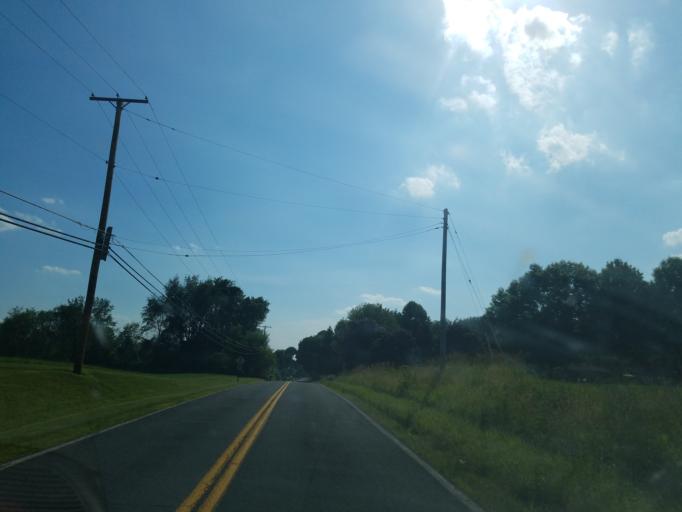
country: US
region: Ohio
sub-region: Portage County
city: Brimfield
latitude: 41.0500
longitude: -81.3385
